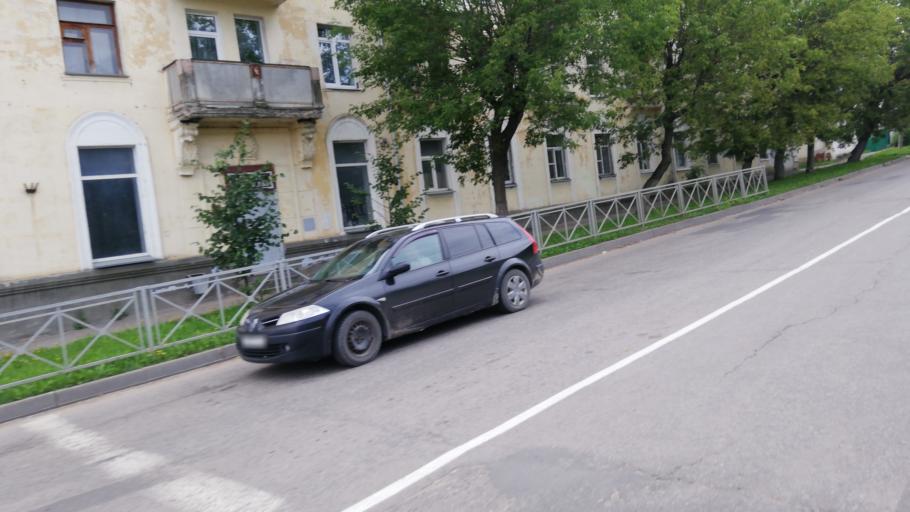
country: RU
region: Kostroma
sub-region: Kostromskoy Rayon
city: Kostroma
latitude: 57.7700
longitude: 40.9181
